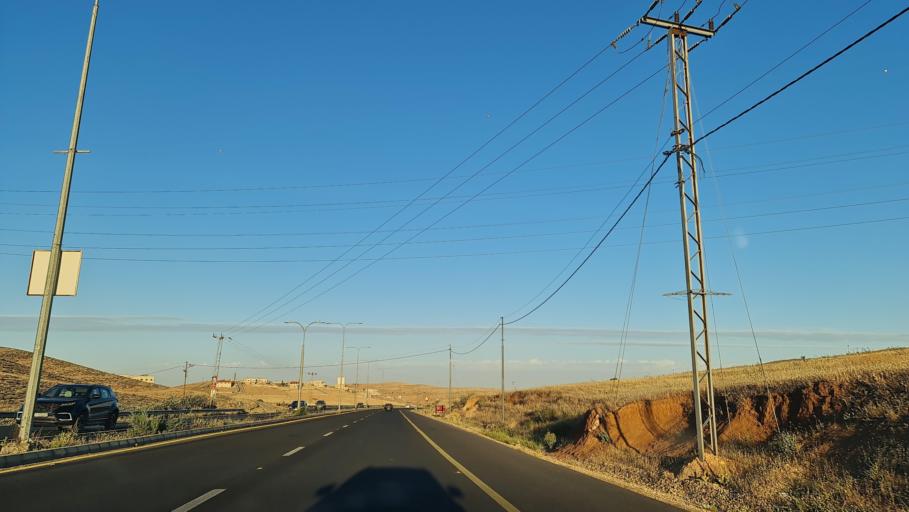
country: JO
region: Zarqa
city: Russeifa
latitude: 32.0877
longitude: 35.9966
